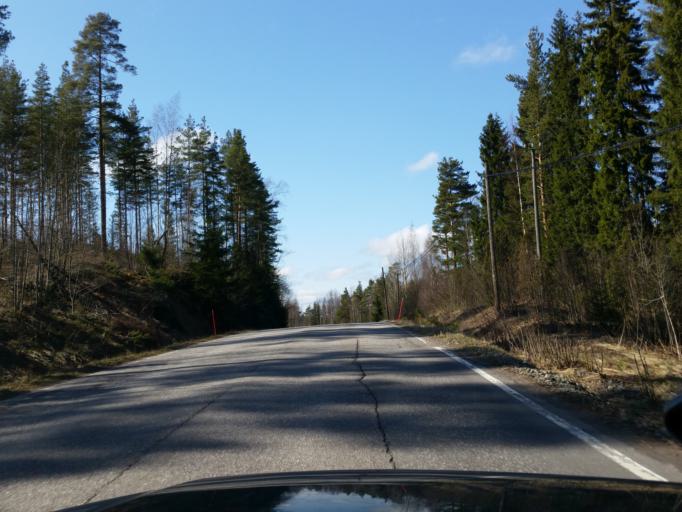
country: FI
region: Uusimaa
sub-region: Helsinki
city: Vihti
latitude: 60.4239
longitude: 24.2656
